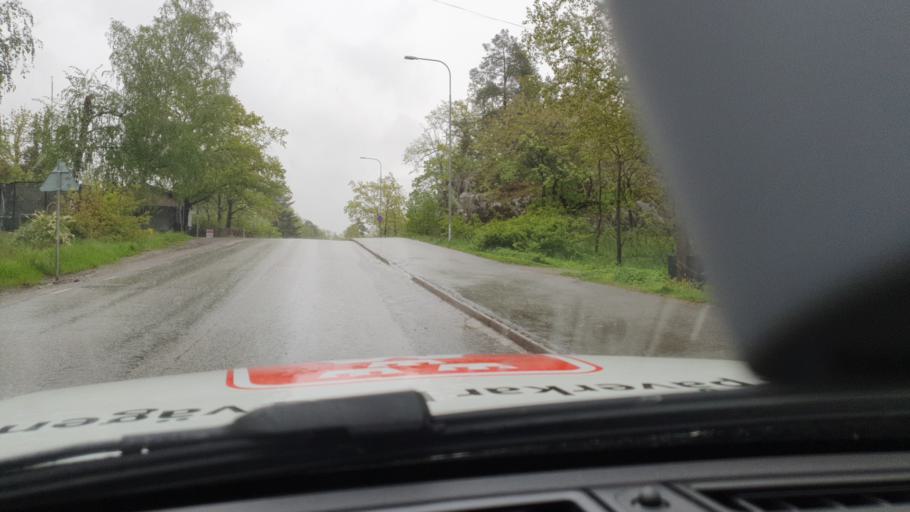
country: SE
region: Stockholm
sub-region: Haninge Kommun
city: Handen
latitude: 59.2262
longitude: 18.1369
